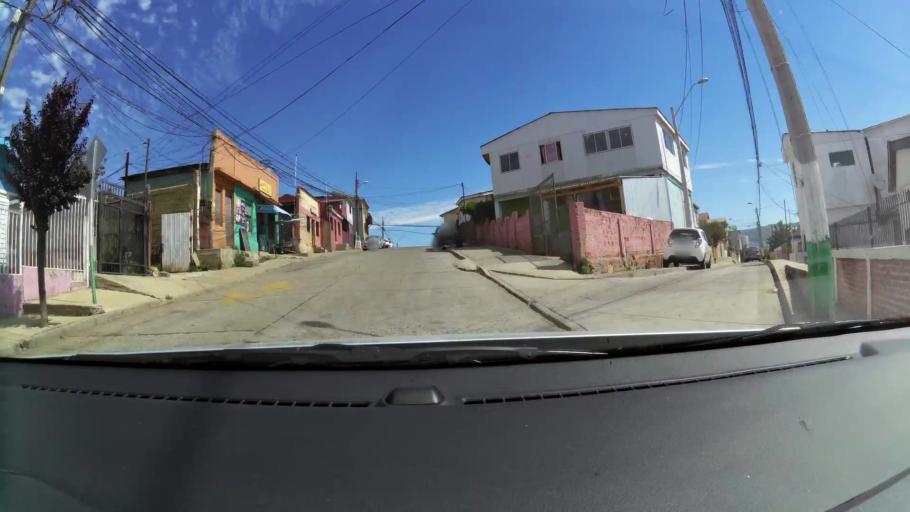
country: CL
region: Valparaiso
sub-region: Provincia de Valparaiso
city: Vina del Mar
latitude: -33.0369
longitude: -71.5828
